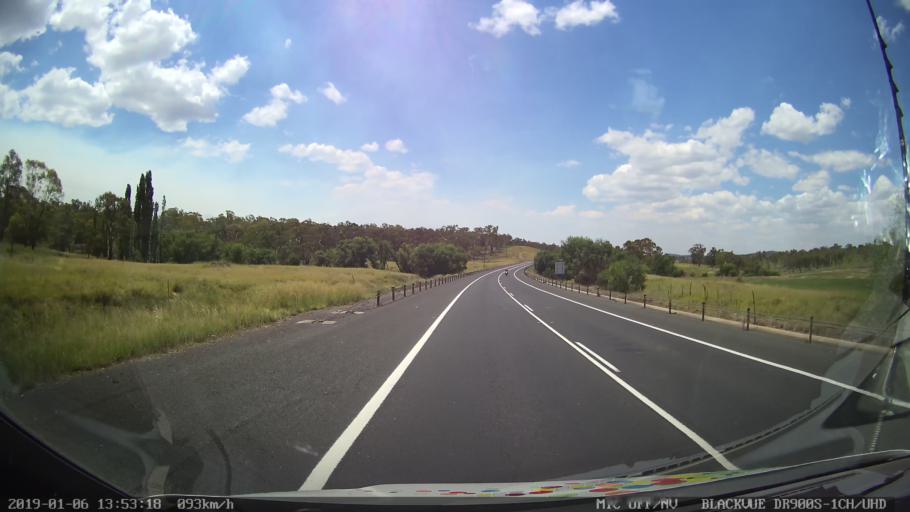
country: AU
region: New South Wales
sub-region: Tamworth Municipality
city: Kootingal
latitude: -30.9095
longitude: 151.1369
